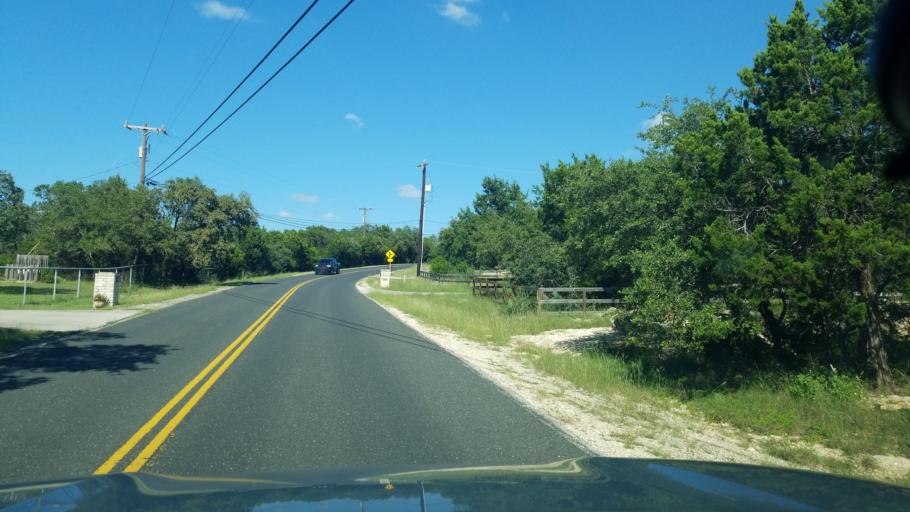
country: US
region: Texas
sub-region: Bexar County
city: Timberwood Park
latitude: 29.6710
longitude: -98.5135
